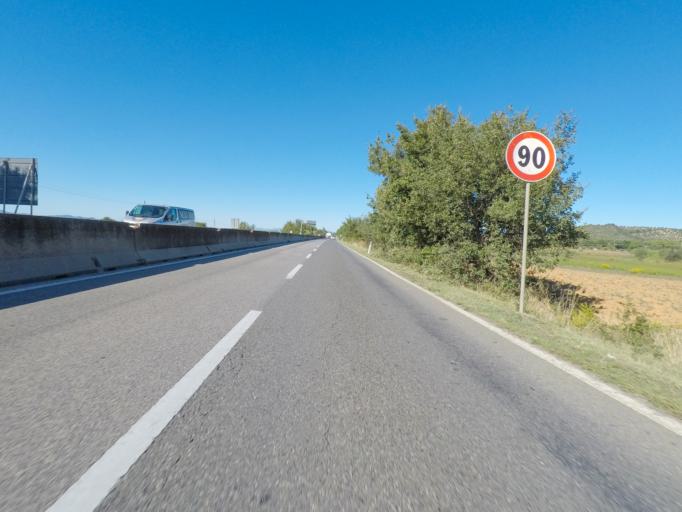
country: IT
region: Tuscany
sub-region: Provincia di Grosseto
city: Grosseto
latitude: 42.6915
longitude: 11.1382
